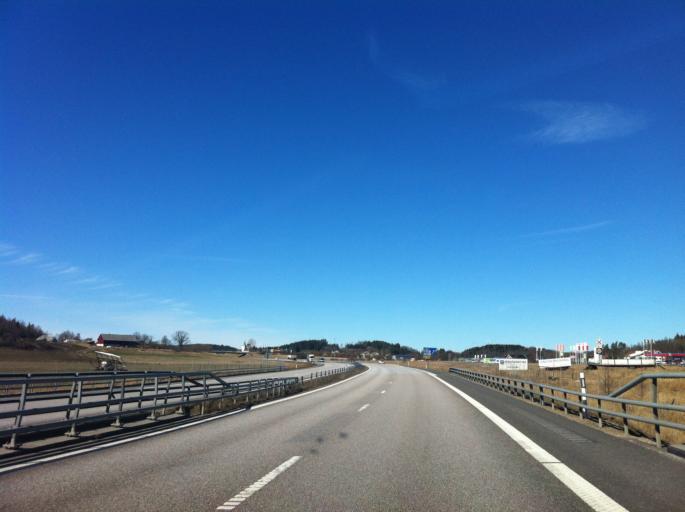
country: SE
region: Vaestra Goetaland
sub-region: Munkedals Kommun
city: Munkedal
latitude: 58.4034
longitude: 11.7410
